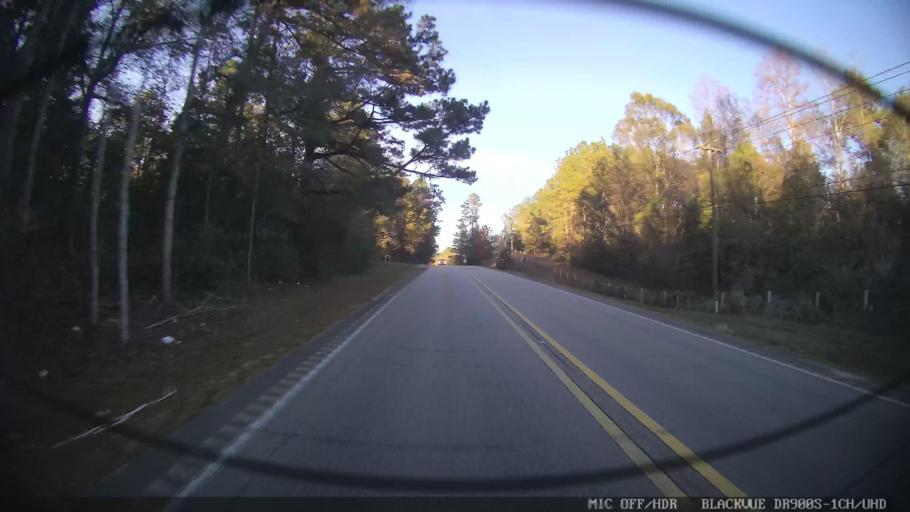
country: US
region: Mississippi
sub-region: Lamar County
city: Purvis
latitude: 31.0778
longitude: -89.4187
